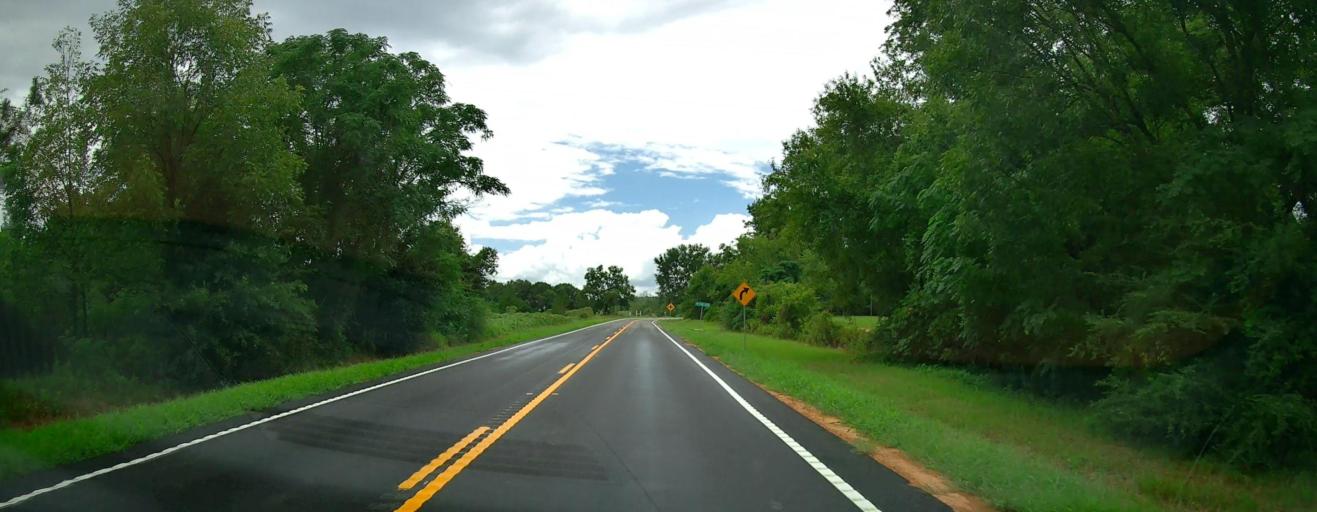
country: US
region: Georgia
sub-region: Wilcox County
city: Rochelle
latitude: 32.0979
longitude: -83.5843
